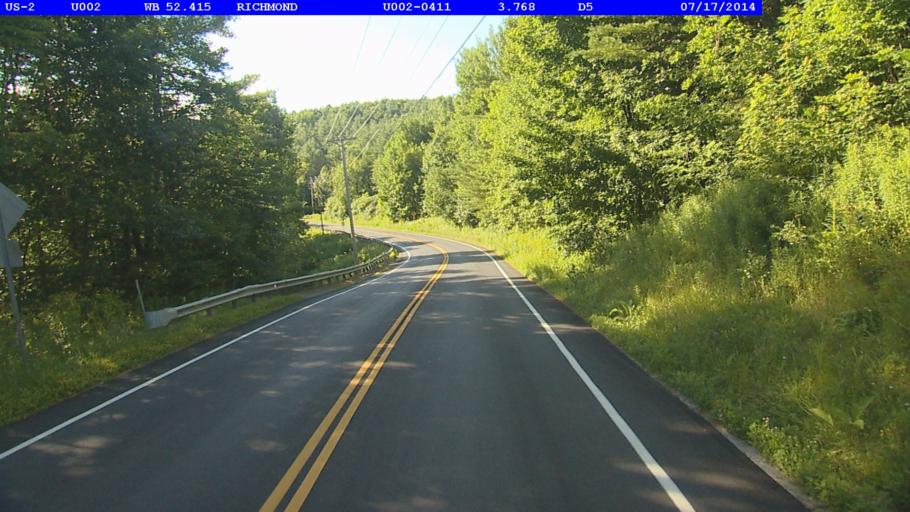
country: US
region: Vermont
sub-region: Chittenden County
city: Williston
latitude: 44.4019
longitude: -72.9759
